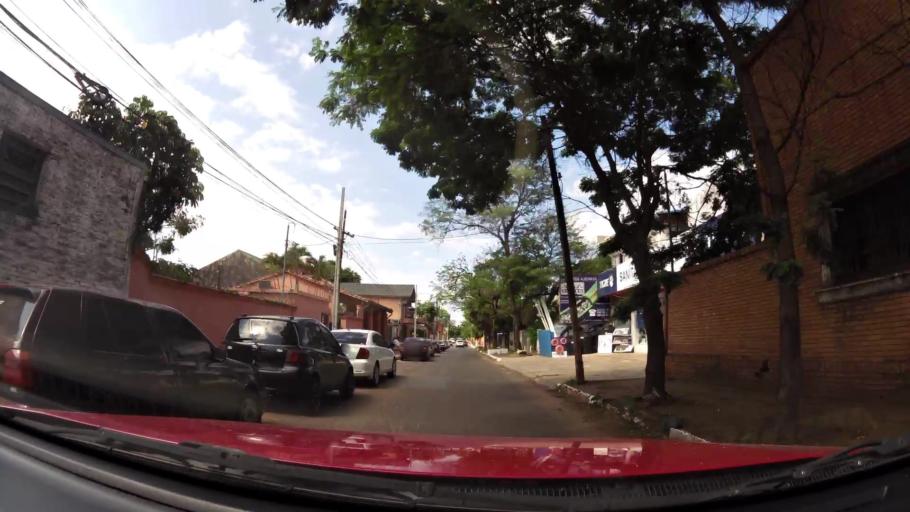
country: PY
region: Central
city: San Lorenzo
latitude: -25.3415
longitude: -57.5122
